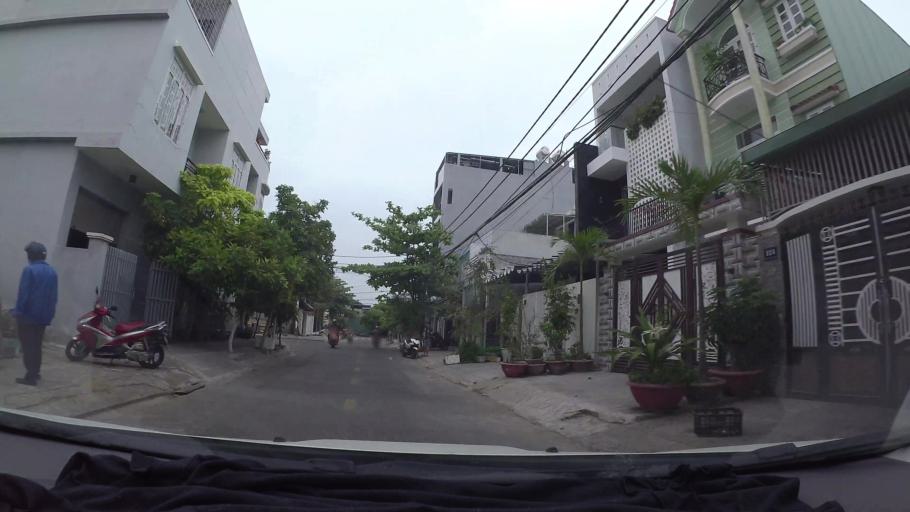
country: VN
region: Da Nang
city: Thanh Khe
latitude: 16.0570
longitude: 108.1755
